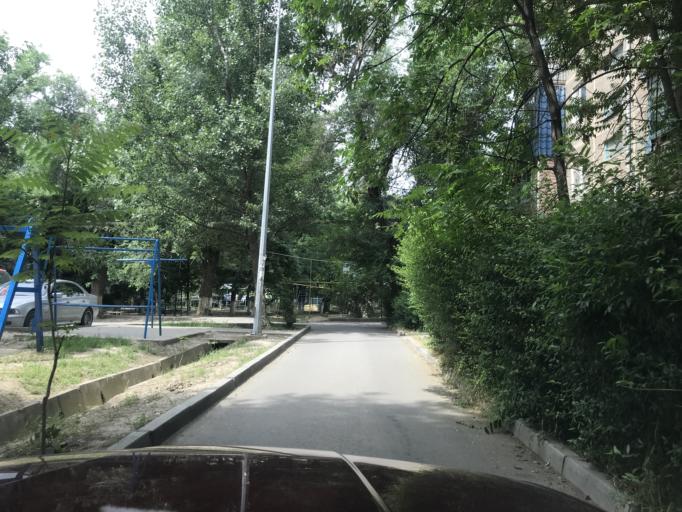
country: KZ
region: Ongtustik Qazaqstan
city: Shymkent
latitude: 42.3106
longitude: 69.5693
